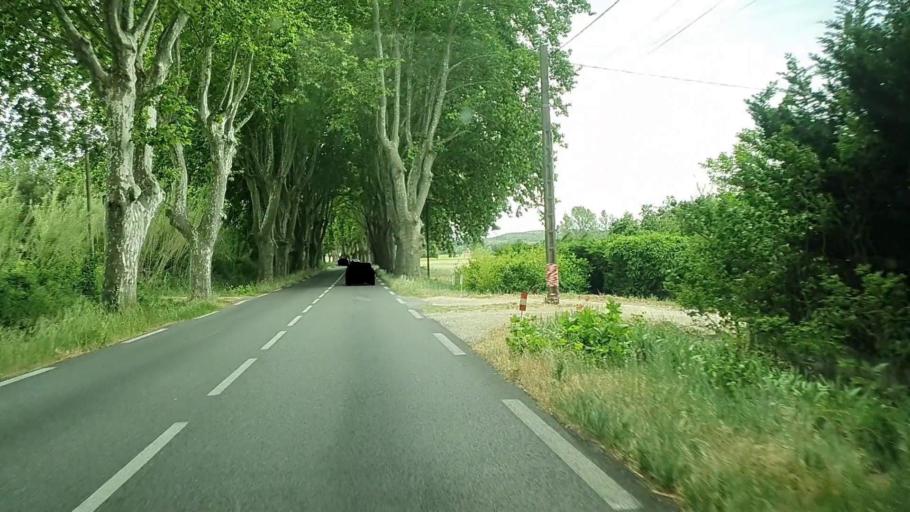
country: FR
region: Languedoc-Roussillon
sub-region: Departement du Gard
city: Bagnols-sur-Ceze
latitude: 44.1297
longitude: 4.6140
